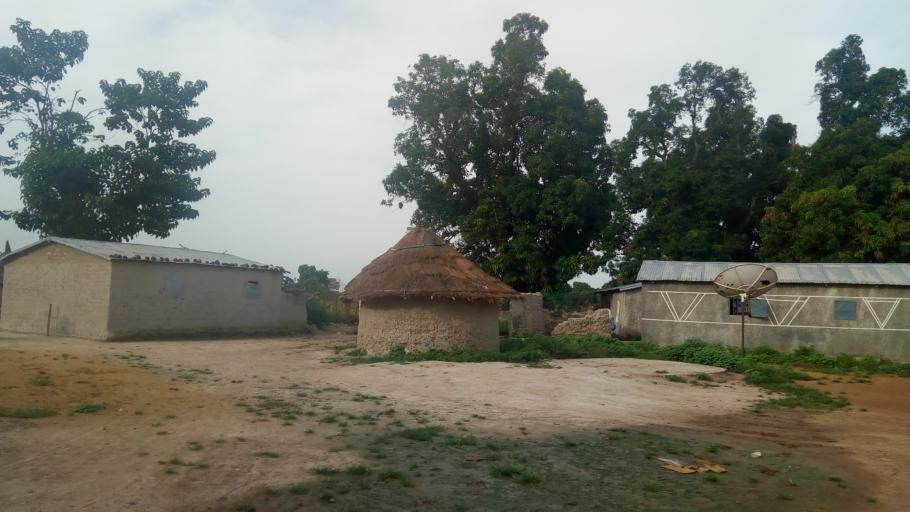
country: ML
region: Koulikoro
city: Kangaba
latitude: 11.6595
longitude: -8.7295
